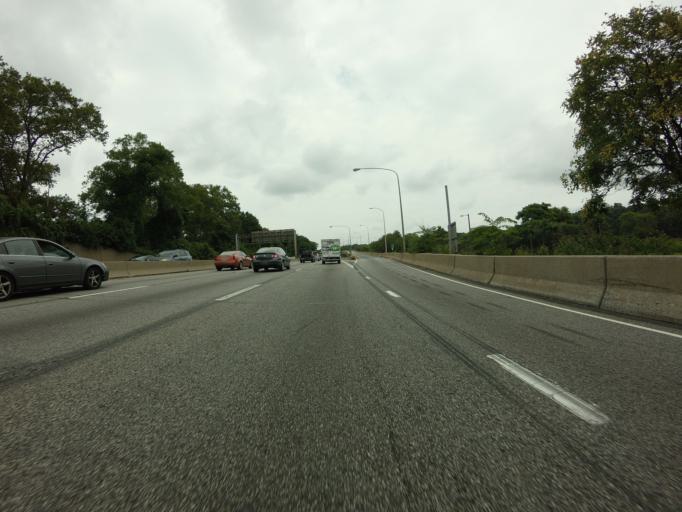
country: US
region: Pennsylvania
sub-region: Philadelphia County
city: Philadelphia
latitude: 39.9713
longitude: -75.1932
